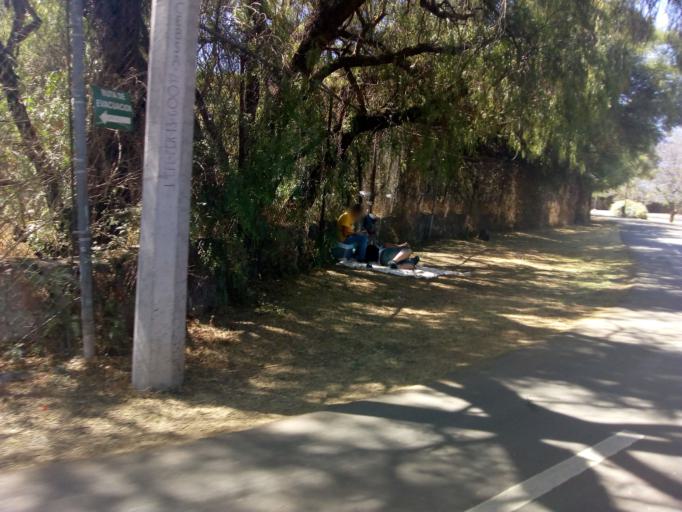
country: MX
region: Guanajuato
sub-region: Leon
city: La Ermita
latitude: 21.1767
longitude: -101.6985
